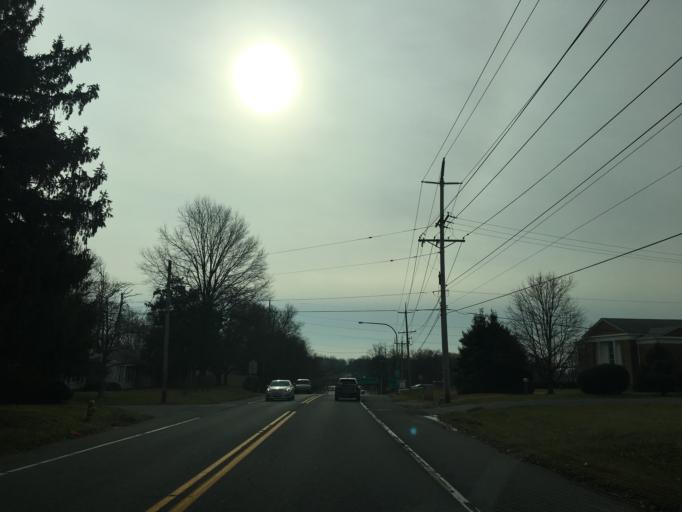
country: US
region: Delaware
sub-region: New Castle County
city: Bellefonte
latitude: 39.7833
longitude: -75.5061
